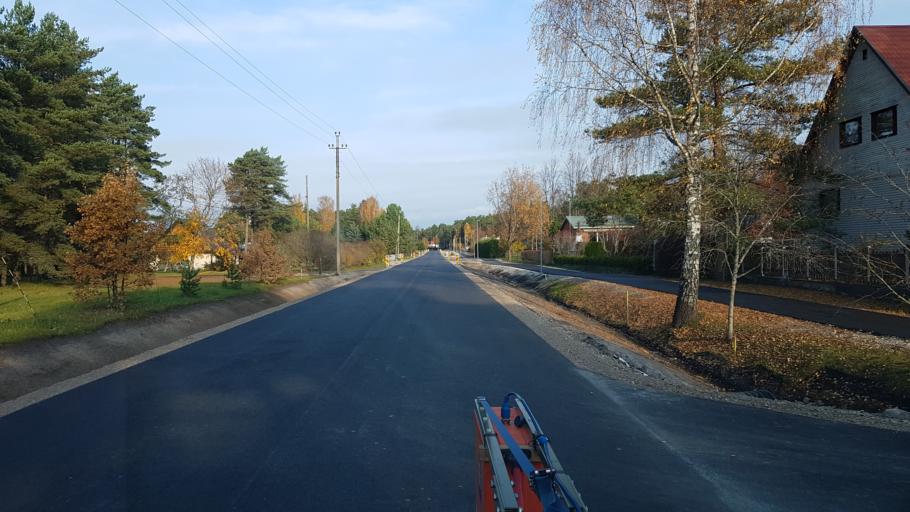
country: EE
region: Paernumaa
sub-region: Paikuse vald
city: Paikuse
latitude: 58.3494
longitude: 24.6209
